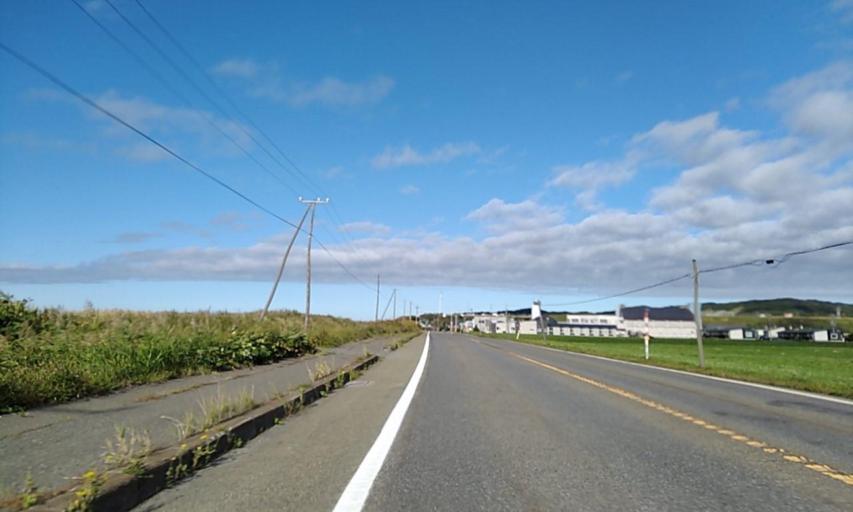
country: JP
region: Hokkaido
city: Shizunai-furukawacho
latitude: 42.2442
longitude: 142.5841
